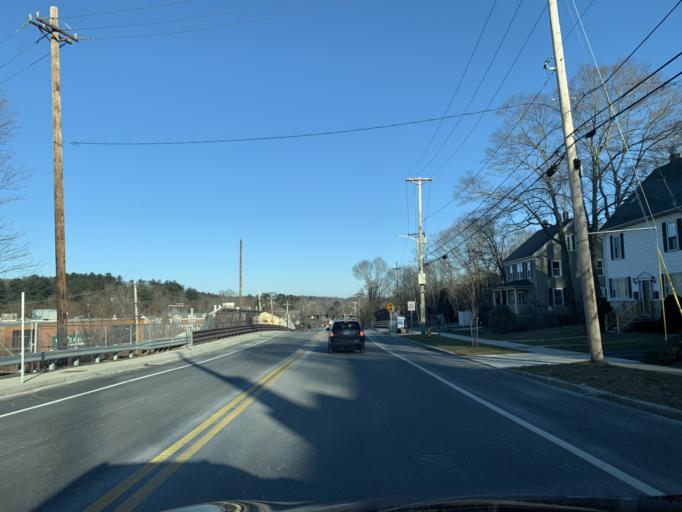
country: US
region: Massachusetts
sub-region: Essex County
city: Andover
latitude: 42.6602
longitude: -71.1433
